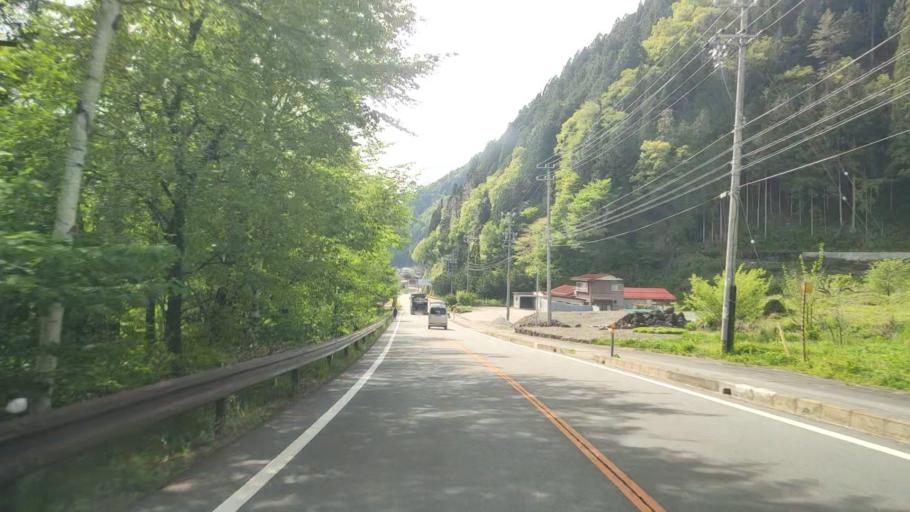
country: JP
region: Gifu
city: Takayama
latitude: 36.2488
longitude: 137.5026
